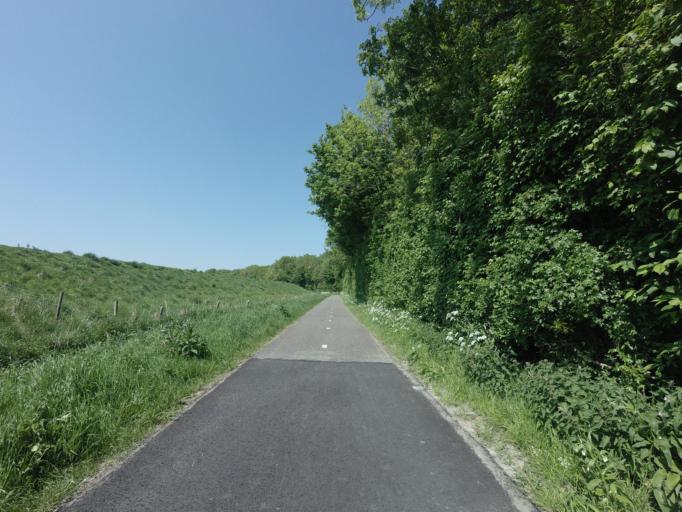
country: NL
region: Zeeland
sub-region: Gemeente Veere
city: Veere
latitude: 51.5287
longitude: 3.6815
